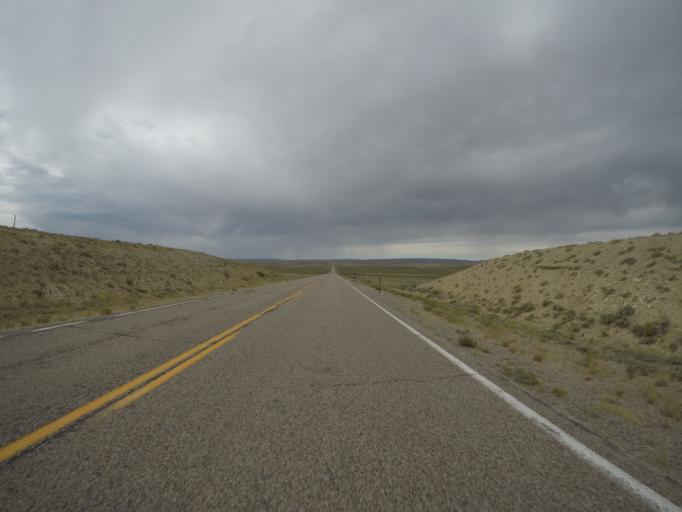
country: US
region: Wyoming
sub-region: Lincoln County
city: Kemmerer
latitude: 41.9633
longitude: -110.1338
